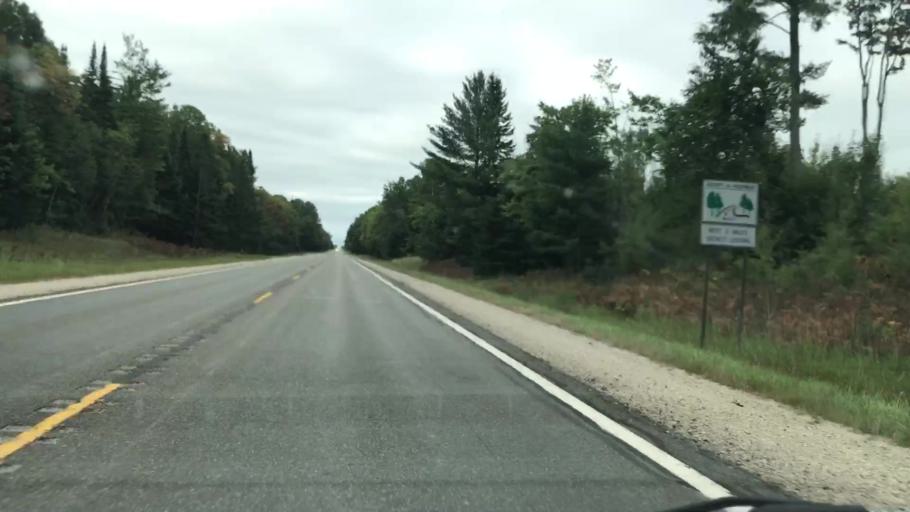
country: US
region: Michigan
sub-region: Luce County
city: Newberry
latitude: 46.2312
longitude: -85.5721
